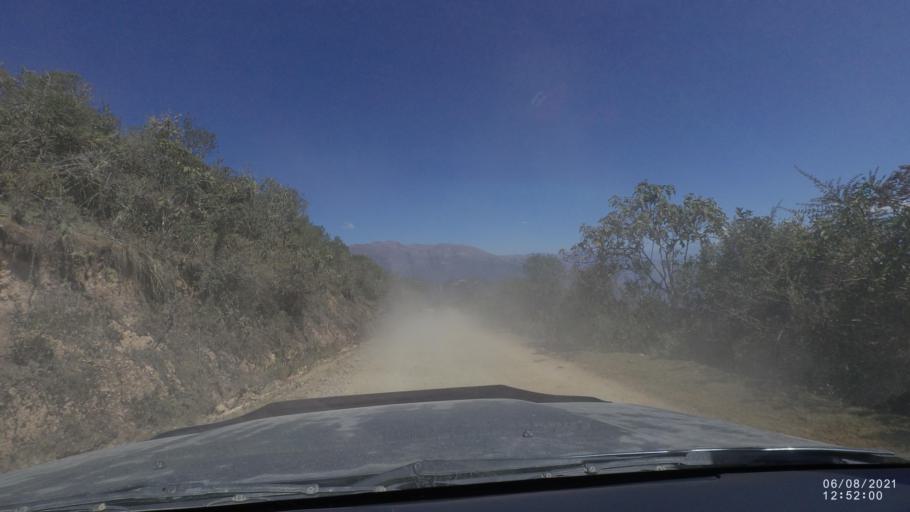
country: BO
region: Cochabamba
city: Colchani
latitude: -16.7621
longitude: -66.6818
